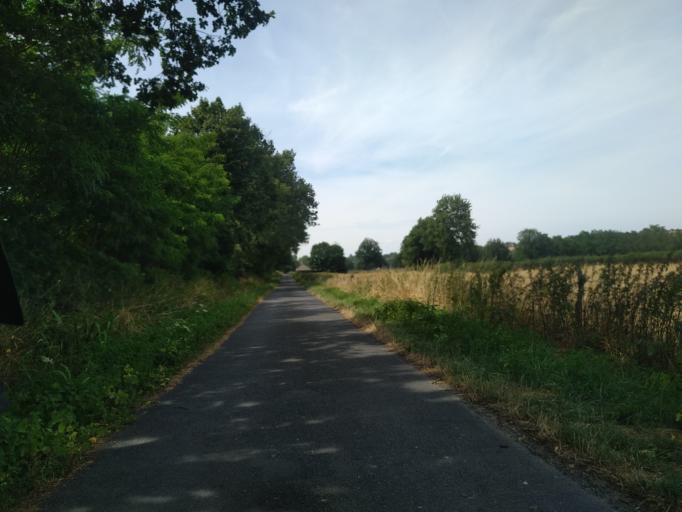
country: FR
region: Auvergne
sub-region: Departement de l'Allier
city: Diou
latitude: 46.5267
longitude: 3.7742
